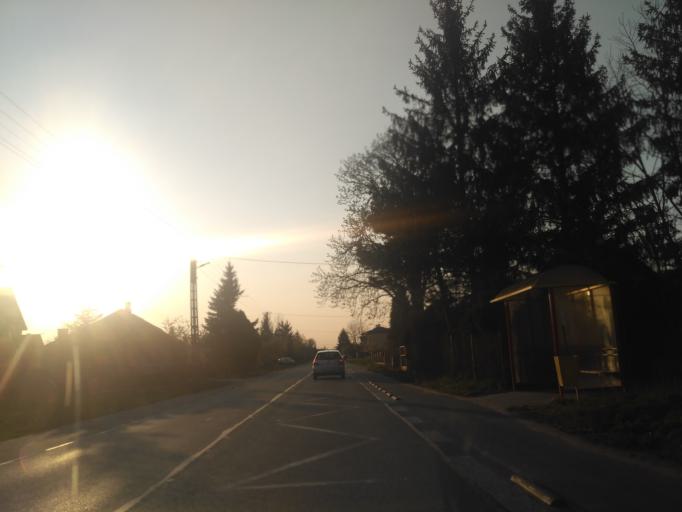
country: PL
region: Lublin Voivodeship
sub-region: Powiat chelmski
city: Pokrowka
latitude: 51.0995
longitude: 23.4822
